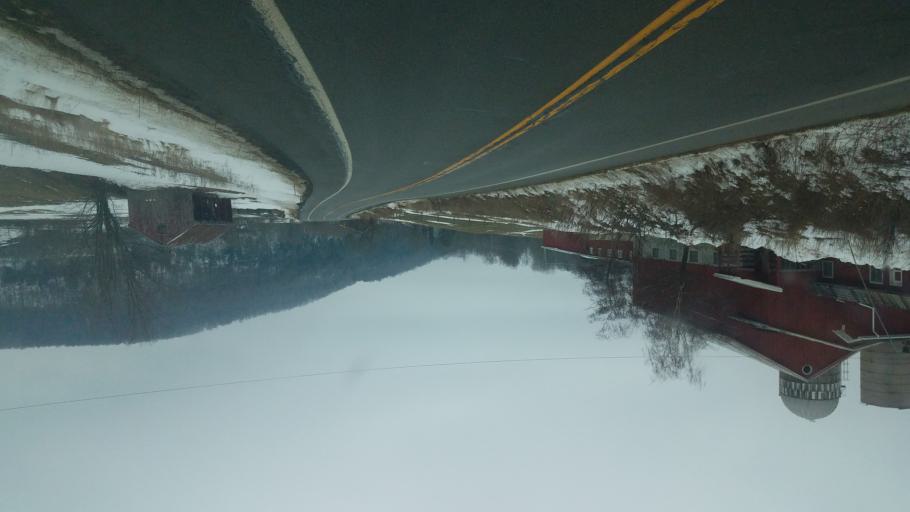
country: US
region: Pennsylvania
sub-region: Tioga County
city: Westfield
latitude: 42.0323
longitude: -77.5376
